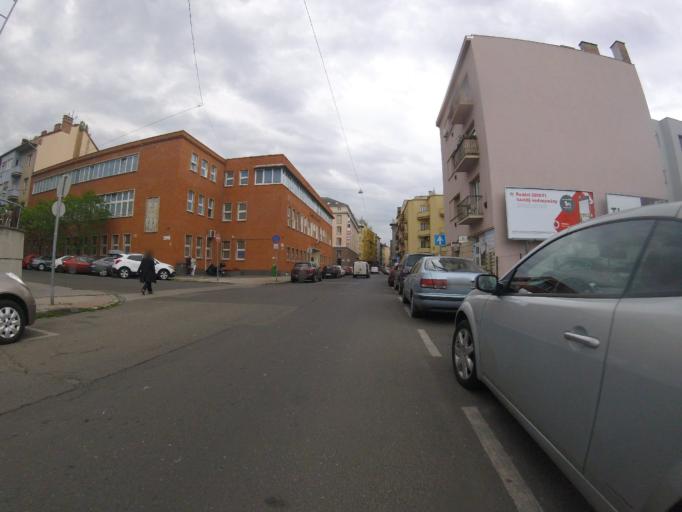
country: HU
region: Budapest
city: Budapest VI. keruelet
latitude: 47.5189
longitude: 19.0584
